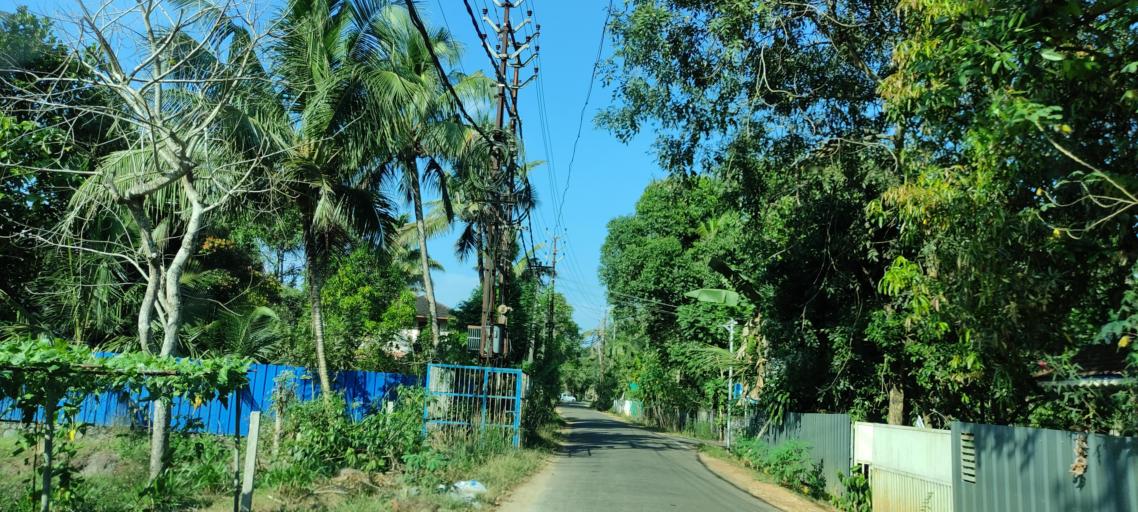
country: IN
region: Kerala
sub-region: Alappuzha
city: Shertallai
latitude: 9.6454
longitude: 76.3457
